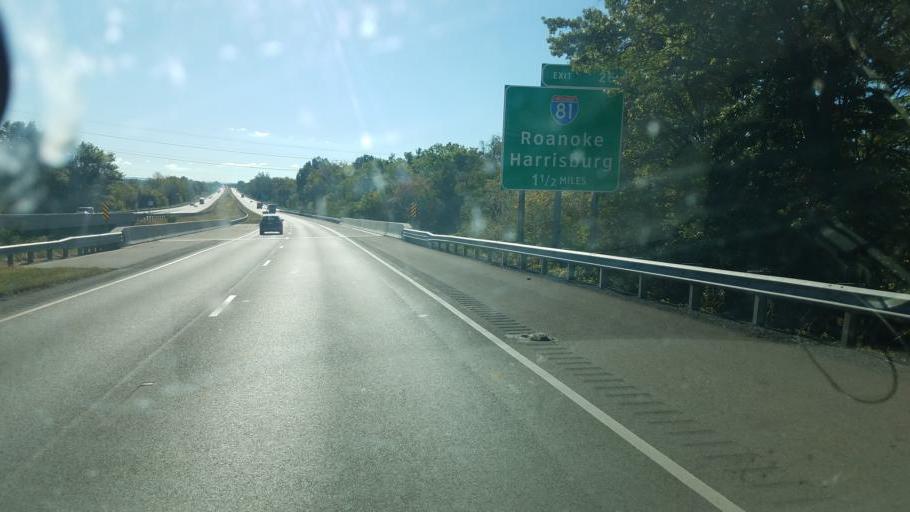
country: US
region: Maryland
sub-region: Washington County
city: Wilson-Conococheague
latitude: 39.6305
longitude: -77.8106
